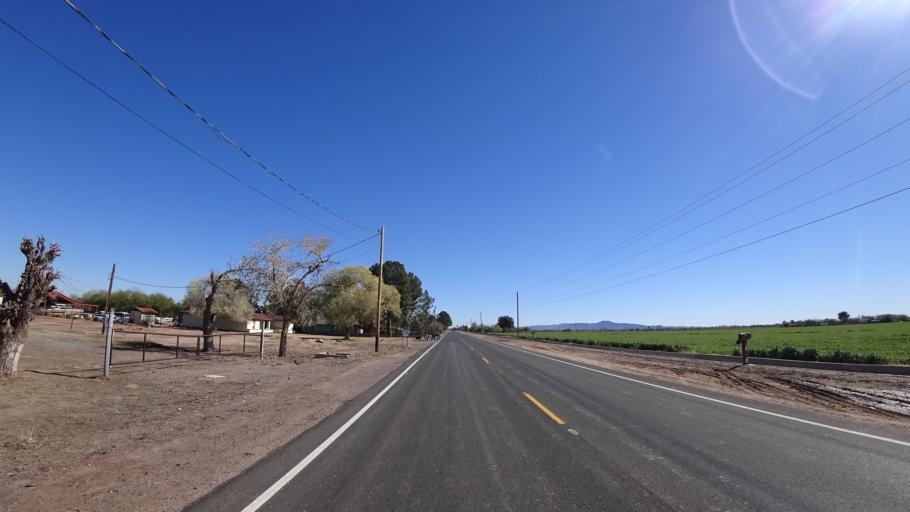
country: US
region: Arizona
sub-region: Maricopa County
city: Avondale
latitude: 33.3919
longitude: -112.2972
